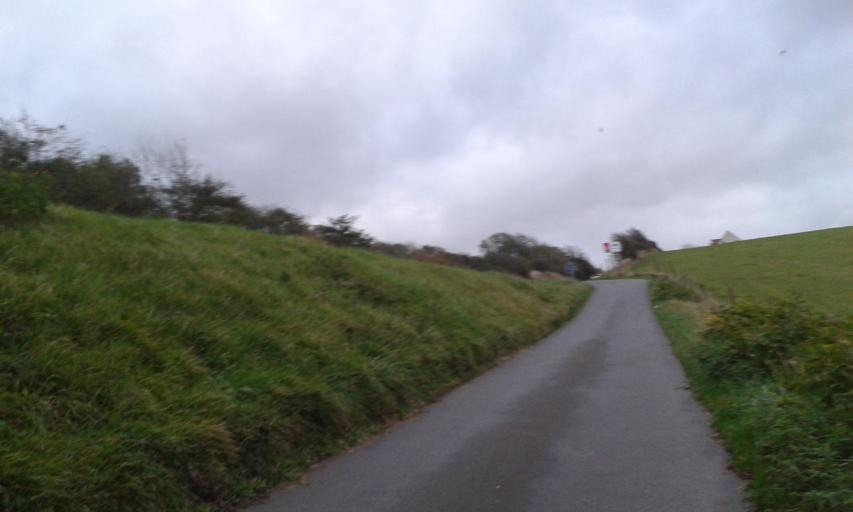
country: FR
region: Nord-Pas-de-Calais
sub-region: Departement du Pas-de-Calais
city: Ferques
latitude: 50.8758
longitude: 1.7359
